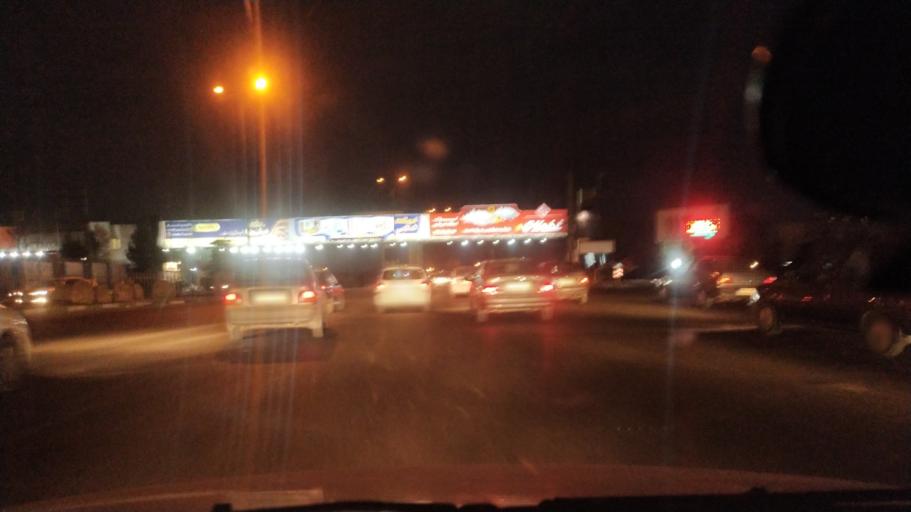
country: IR
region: Alborz
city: Karaj
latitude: 35.7874
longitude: 51.0055
